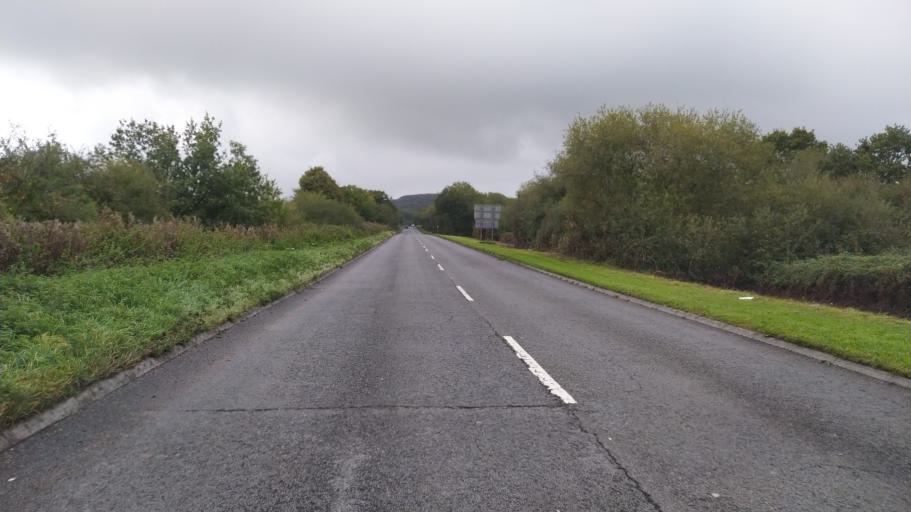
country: GB
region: England
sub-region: Dorset
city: Shaftesbury
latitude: 51.0453
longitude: -2.1841
